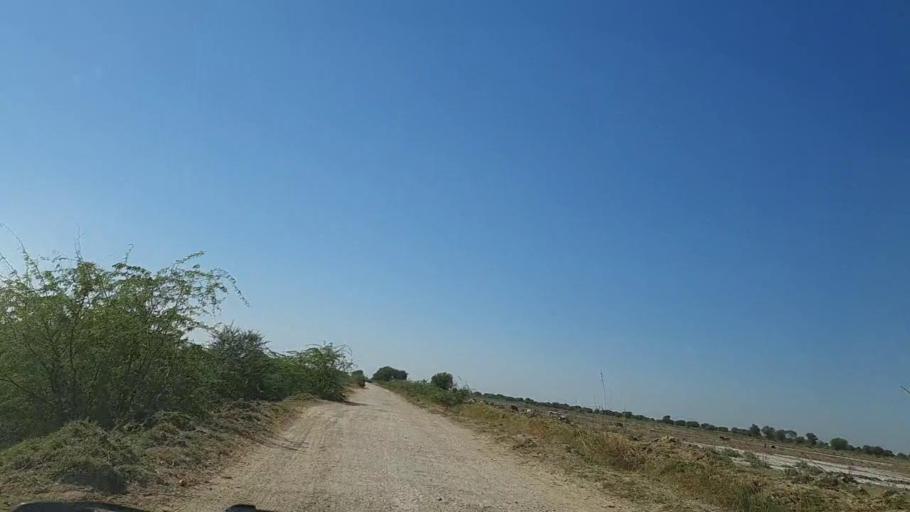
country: PK
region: Sindh
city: Pithoro
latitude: 25.5617
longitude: 69.4615
